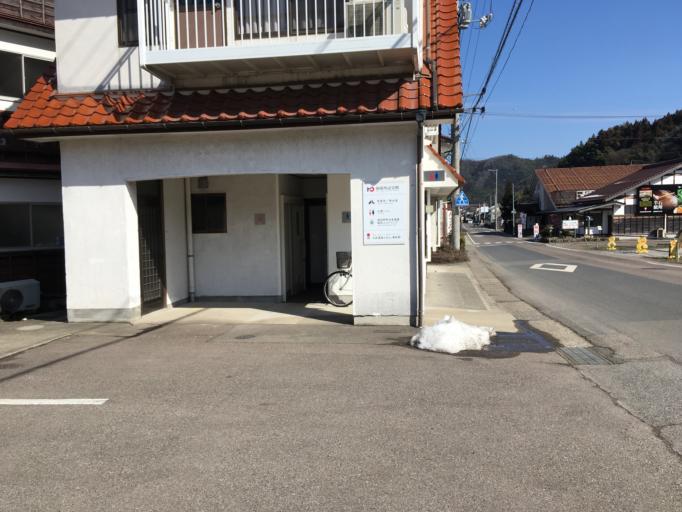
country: JP
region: Shimane
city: Masuda
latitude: 34.4573
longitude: 131.7689
